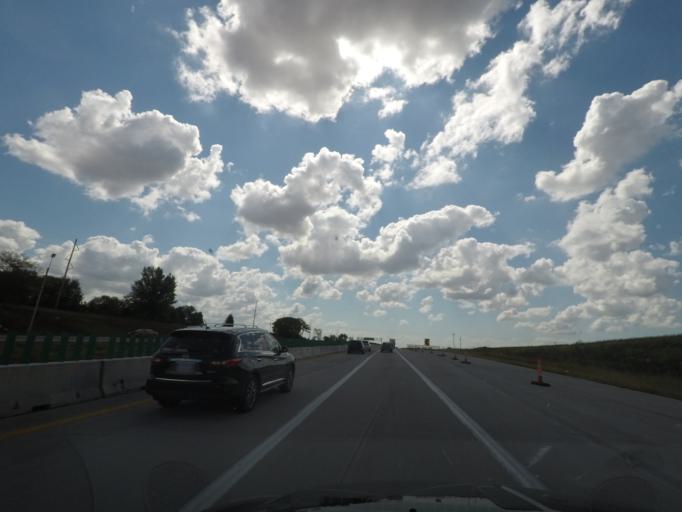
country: US
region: Iowa
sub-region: Story County
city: Huxley
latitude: 41.9524
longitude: -93.5701
